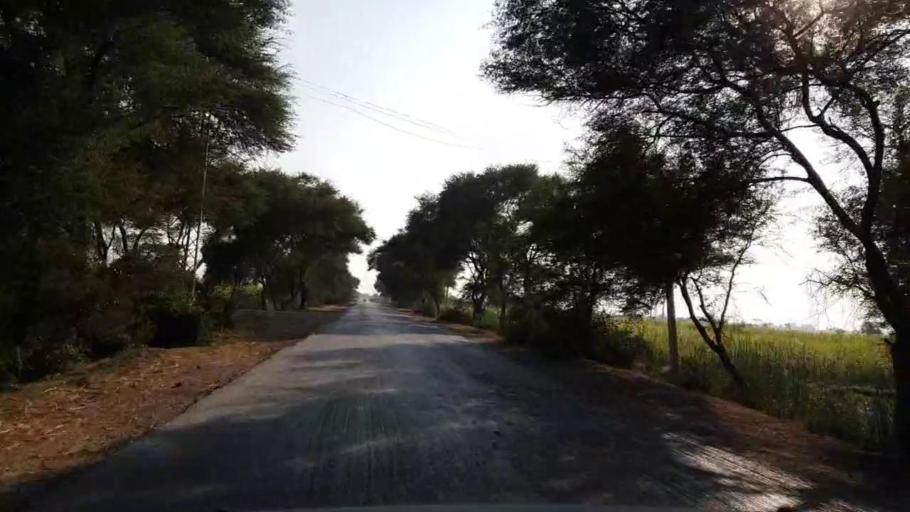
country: PK
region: Sindh
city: Bulri
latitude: 24.8731
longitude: 68.3395
